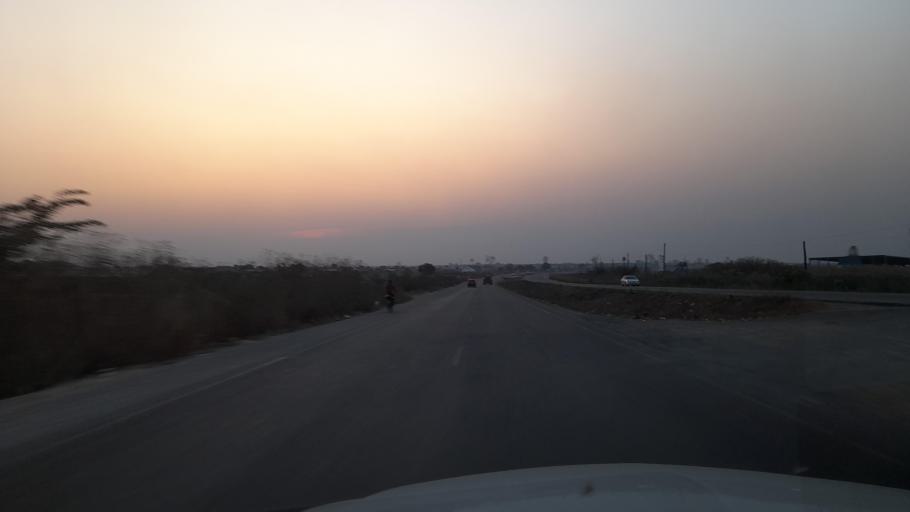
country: ZM
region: Copperbelt
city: Kitwe
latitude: -12.7648
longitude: 28.1727
